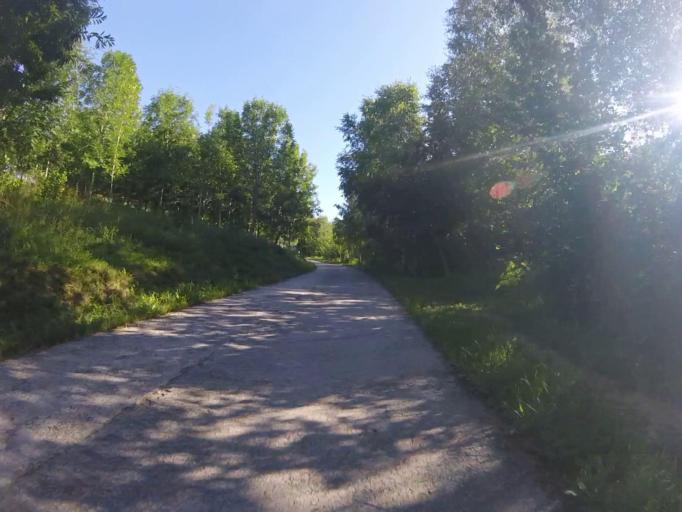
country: ES
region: Basque Country
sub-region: Provincia de Guipuzcoa
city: Fuenterrabia
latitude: 43.3715
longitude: -1.8192
